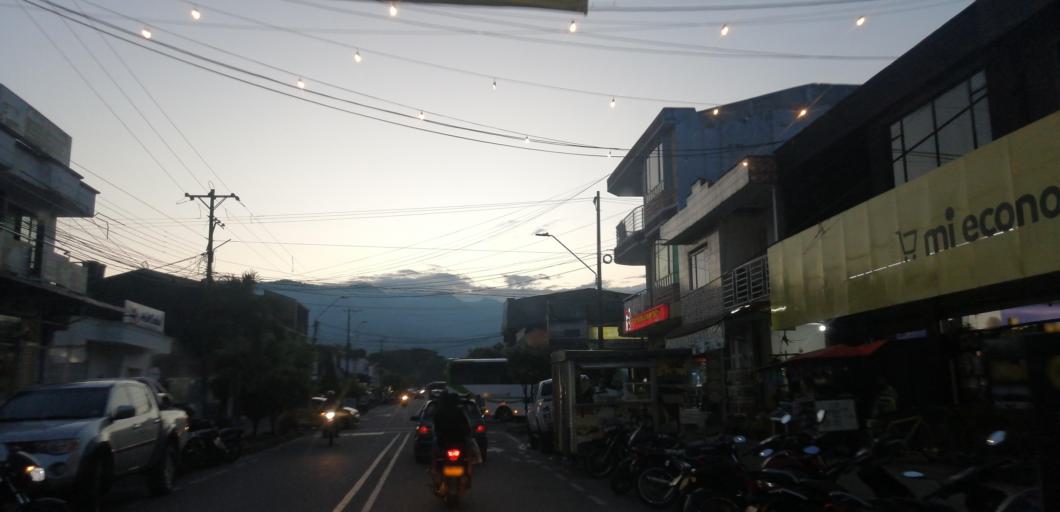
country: CO
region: Meta
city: Acacias
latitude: 3.9882
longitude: -73.7747
